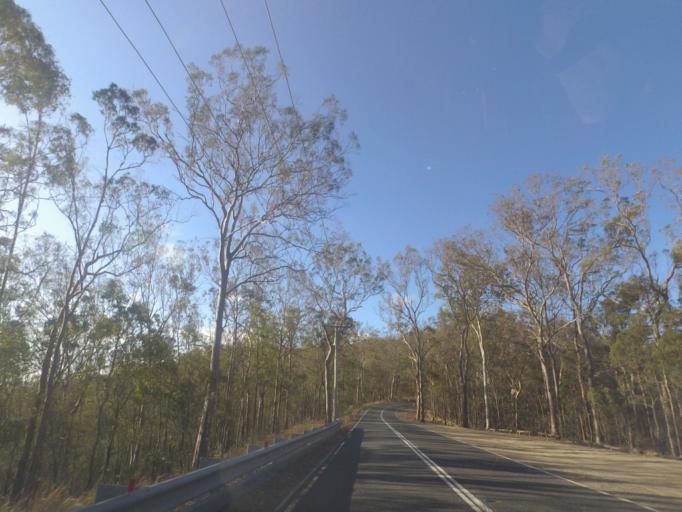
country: AU
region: Queensland
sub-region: Brisbane
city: Taringa
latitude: -27.4820
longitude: 152.9540
